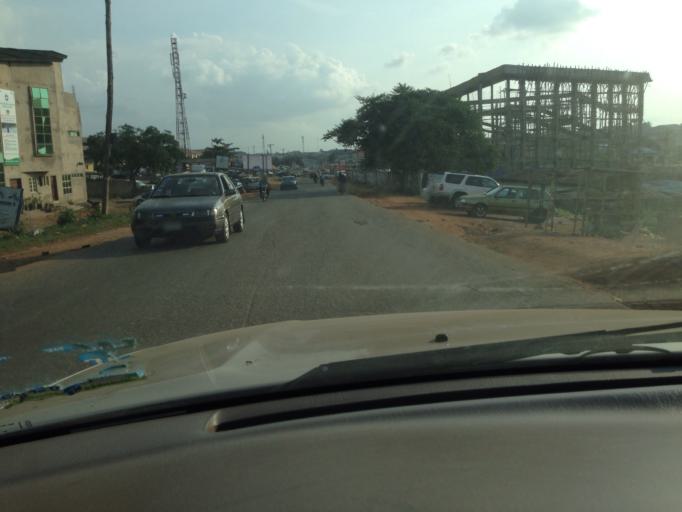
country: NG
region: Oyo
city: Ibadan
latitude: 7.4376
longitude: 3.9479
